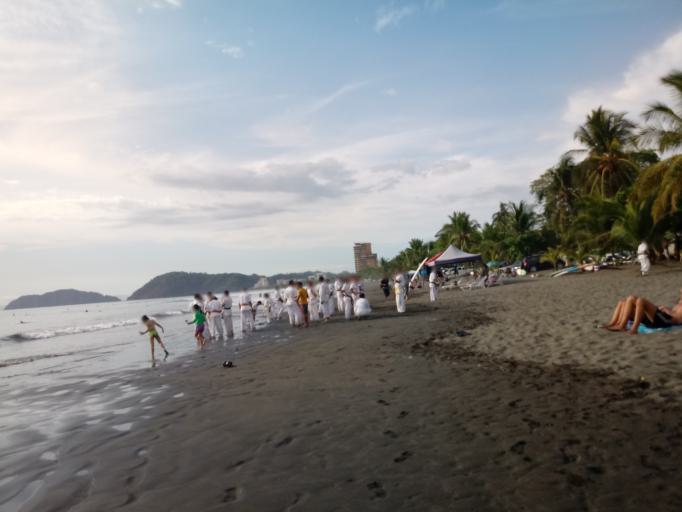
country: CR
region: Puntarenas
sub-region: Canton de Garabito
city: Jaco
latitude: 9.6033
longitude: -84.6220
